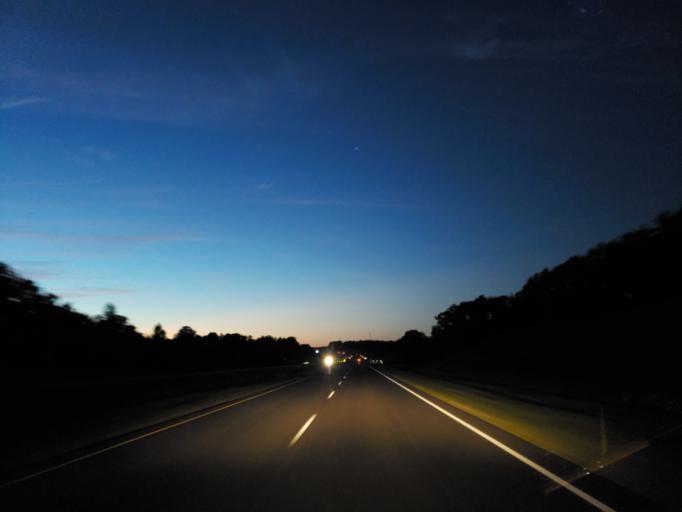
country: US
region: Mississippi
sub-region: Clarke County
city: Quitman
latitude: 32.0950
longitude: -88.7022
